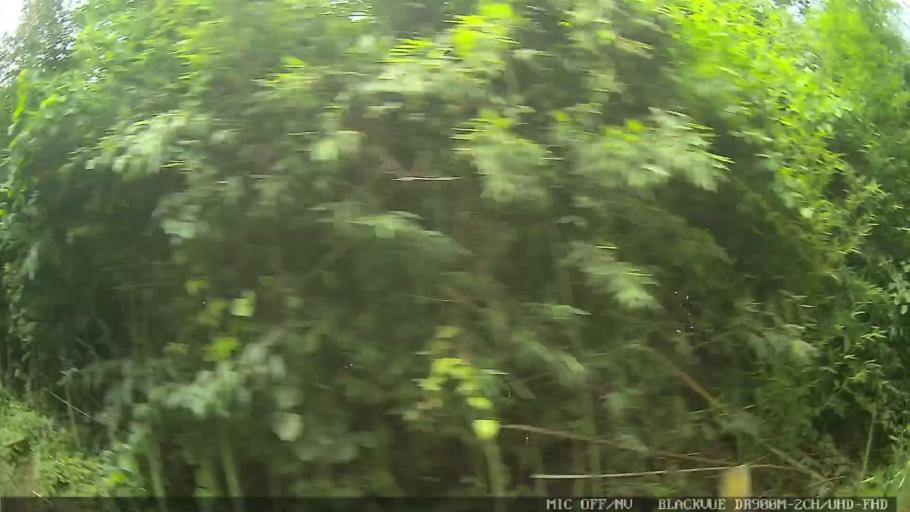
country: BR
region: Sao Paulo
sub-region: Mogi das Cruzes
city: Mogi das Cruzes
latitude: -23.5483
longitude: -46.1504
